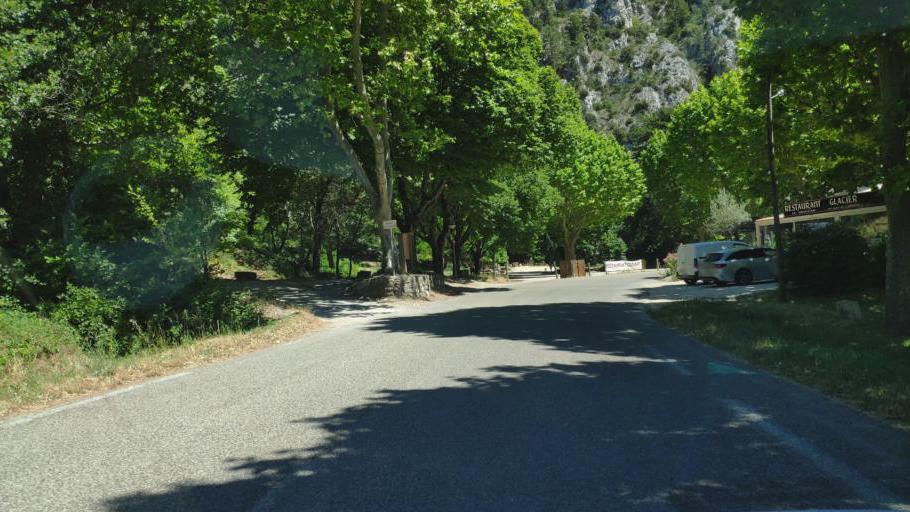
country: FR
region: Provence-Alpes-Cote d'Azur
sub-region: Departement du Vaucluse
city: Malaucene
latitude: 44.1674
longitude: 5.1482
